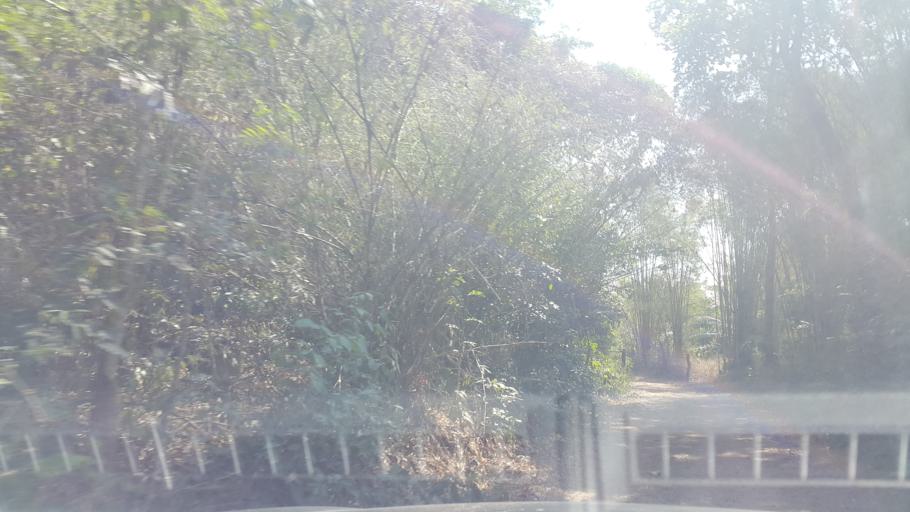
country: TH
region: Sukhothai
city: Thung Saliam
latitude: 17.3423
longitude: 99.5845
